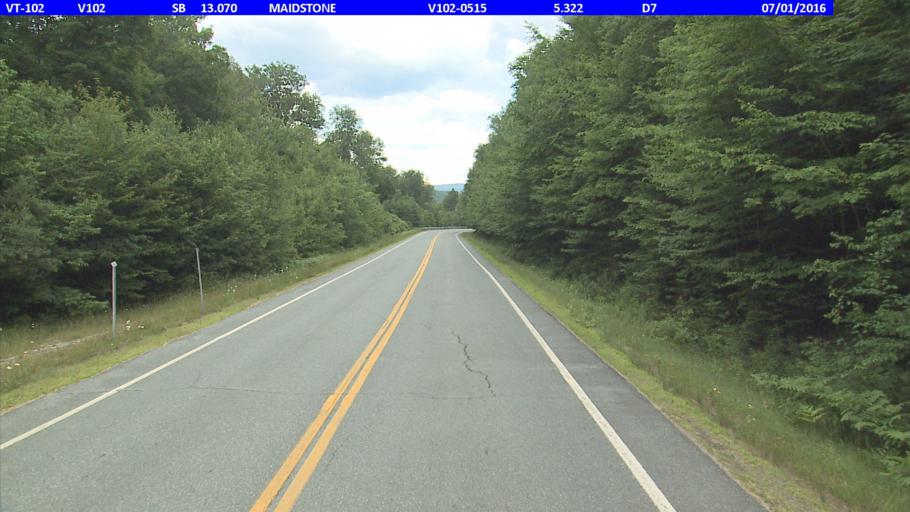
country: US
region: New Hampshire
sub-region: Coos County
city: Stratford
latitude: 44.6355
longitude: -71.5628
